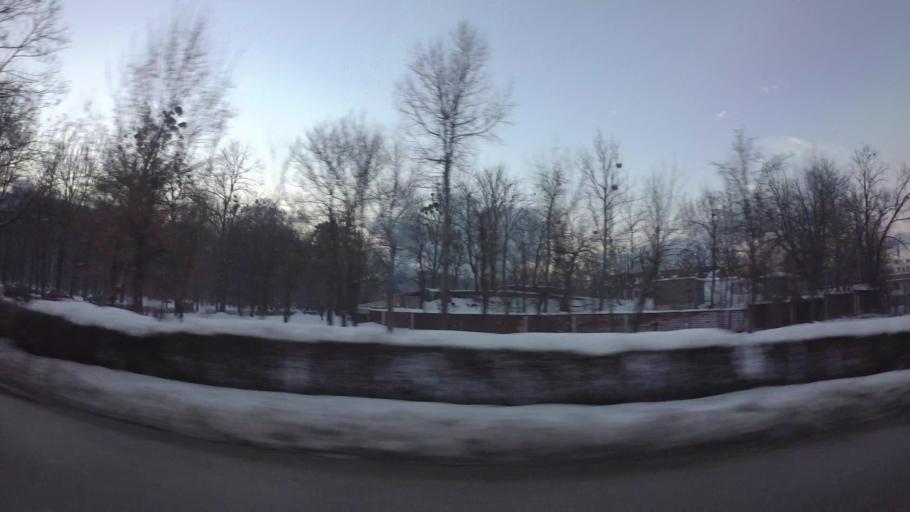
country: BA
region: Federation of Bosnia and Herzegovina
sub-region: Kanton Sarajevo
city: Sarajevo
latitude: 43.8252
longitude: 18.3078
